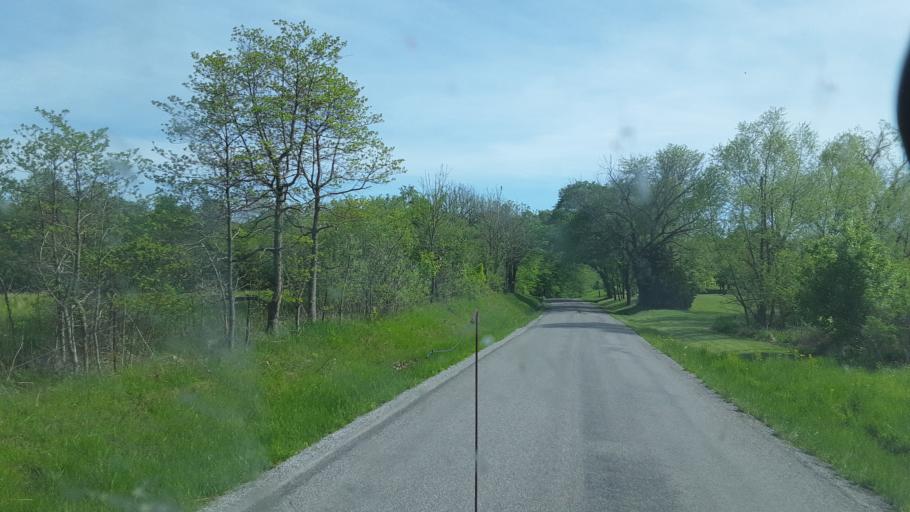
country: US
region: Illinois
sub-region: Jackson County
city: Carbondale
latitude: 37.6802
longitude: -89.2953
